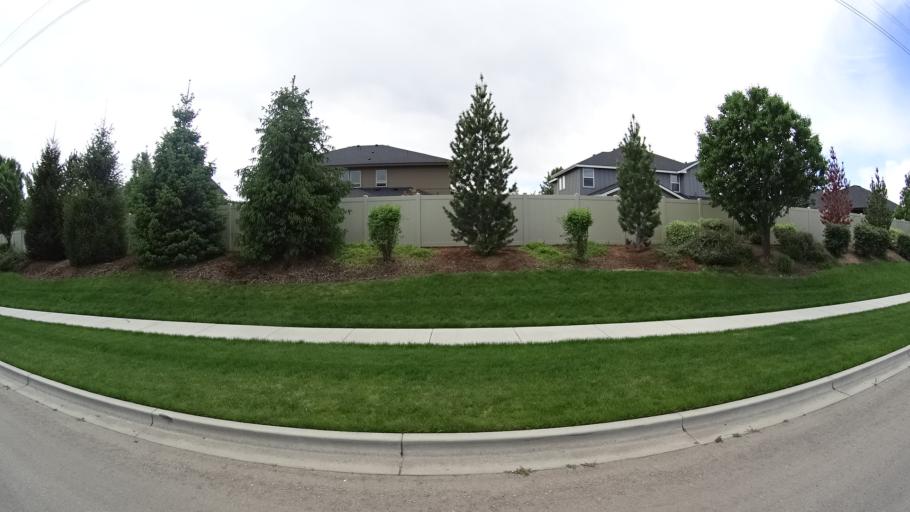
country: US
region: Idaho
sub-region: Ada County
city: Meridian
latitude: 43.5757
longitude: -116.3510
